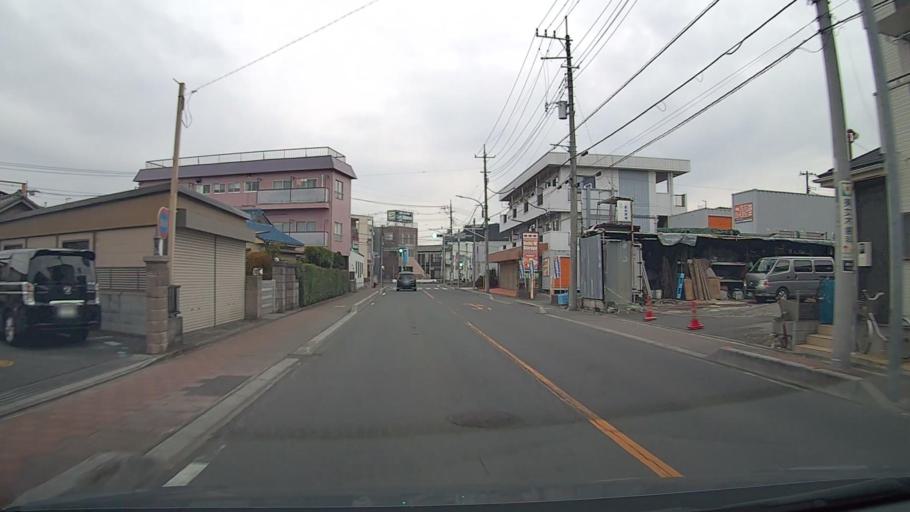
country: JP
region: Saitama
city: Wako
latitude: 35.8297
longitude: 139.6415
